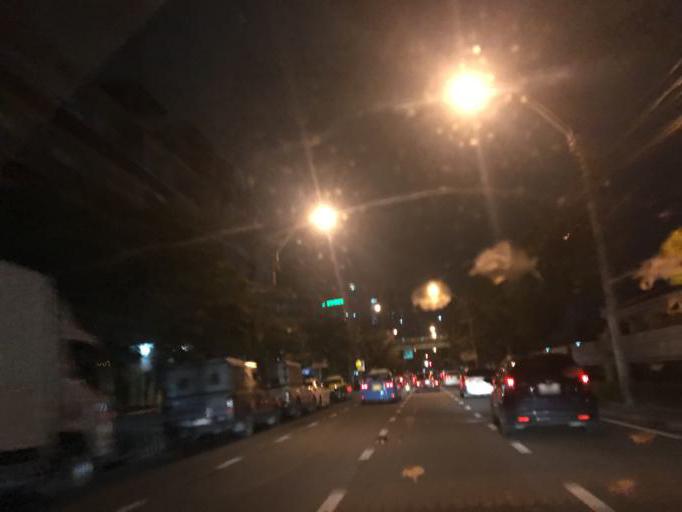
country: TH
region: Bangkok
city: Pom Prap Sattru Phai
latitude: 13.7459
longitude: 100.5143
